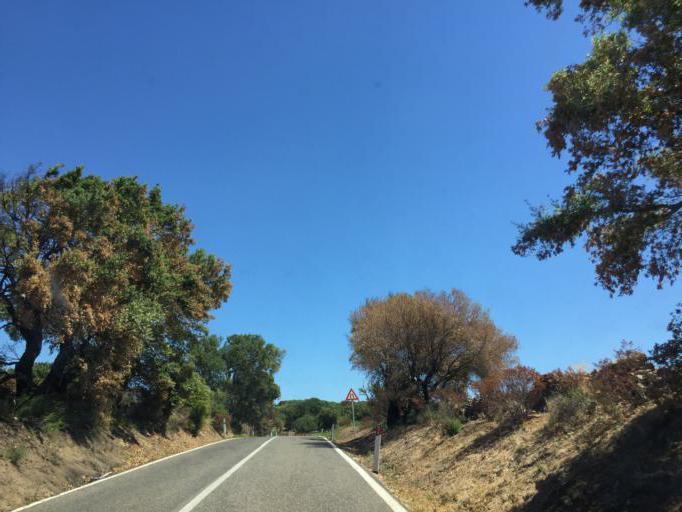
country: IT
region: Sardinia
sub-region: Provincia di Olbia-Tempio
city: Telti
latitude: 40.8925
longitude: 9.3070
